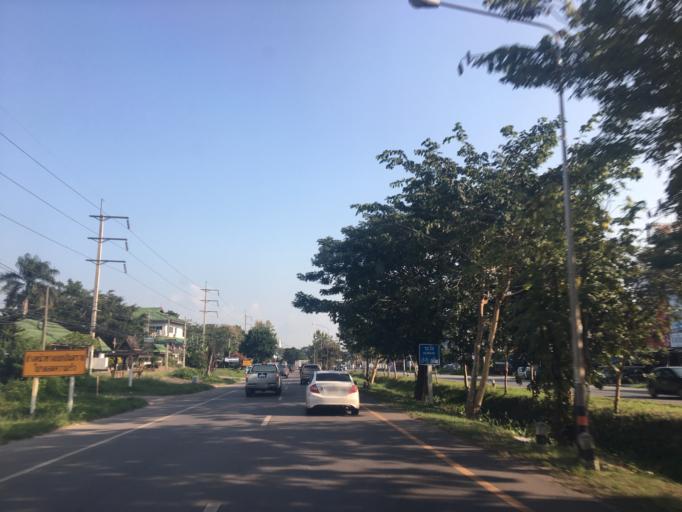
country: TH
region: Phayao
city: Phayao
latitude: 19.1676
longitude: 99.9095
